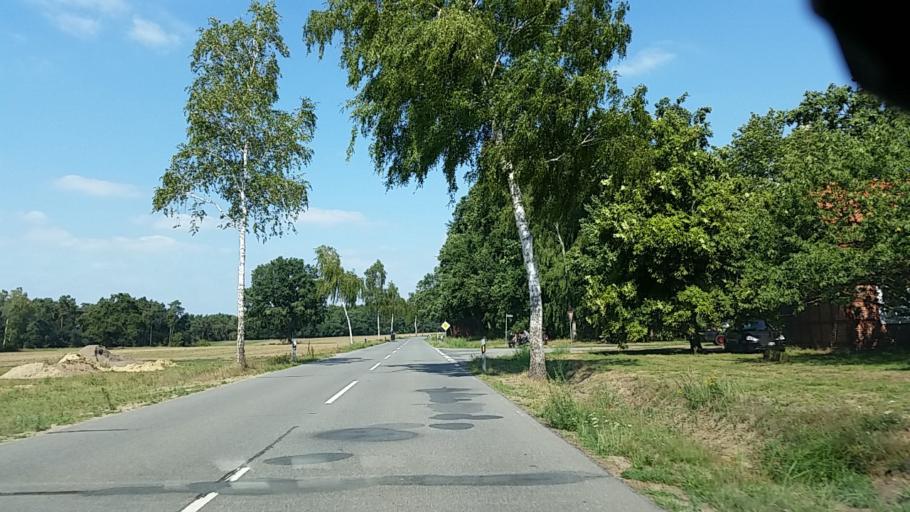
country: DE
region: Lower Saxony
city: Jelmstorf
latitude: 53.1264
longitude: 10.5332
